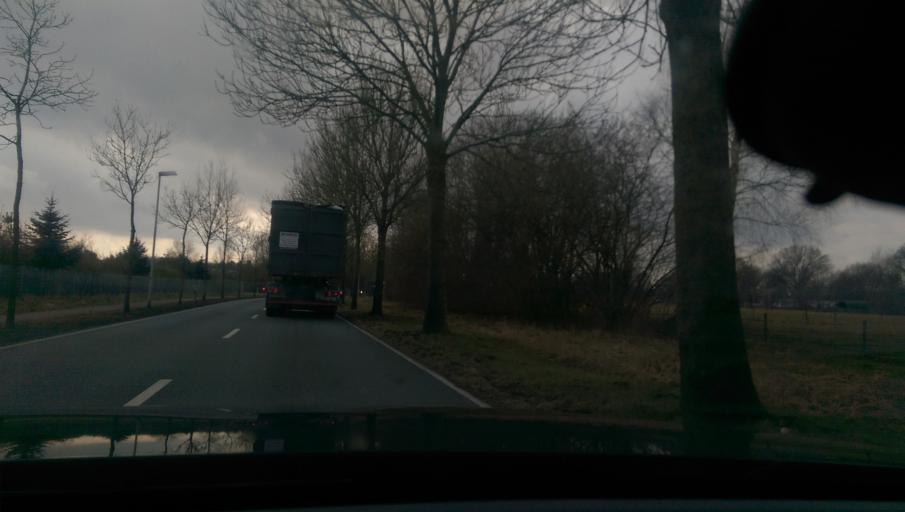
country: DE
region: Lower Saxony
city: Verden
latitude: 52.9163
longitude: 9.2749
